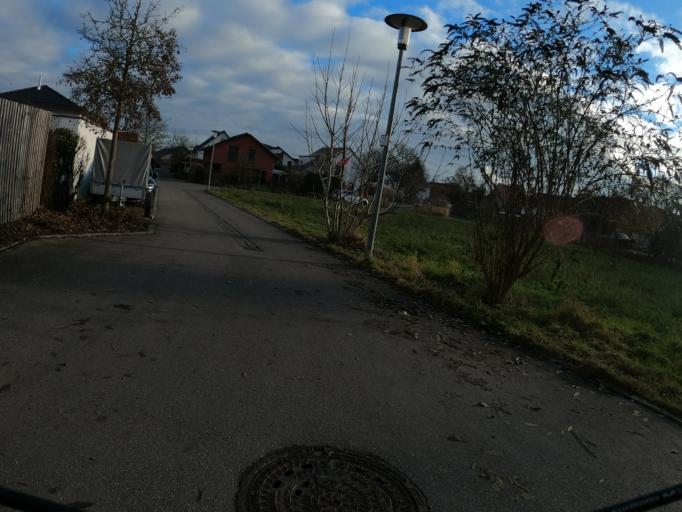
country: DE
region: Bavaria
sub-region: Swabia
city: Nersingen
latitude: 48.4599
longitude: 10.1060
